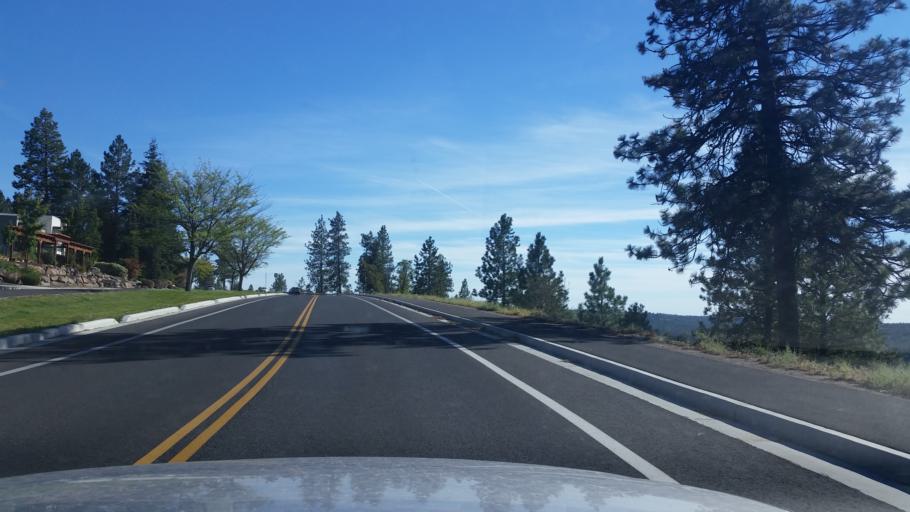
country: US
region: Washington
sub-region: Spokane County
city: Spokane
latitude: 47.6250
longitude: -117.4291
